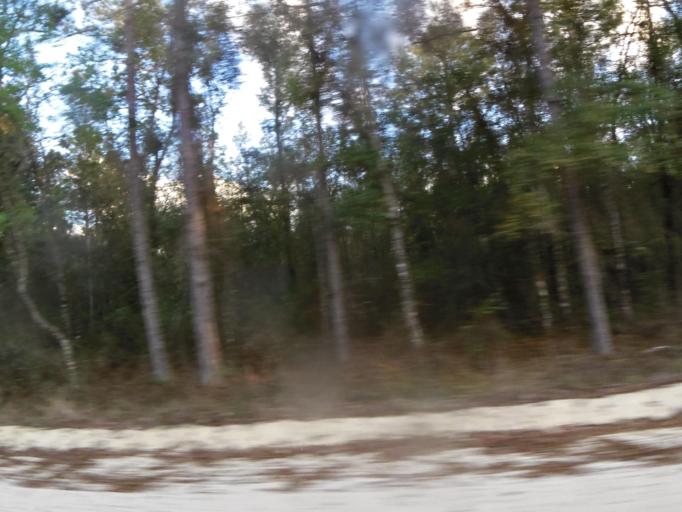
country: US
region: Florida
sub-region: Putnam County
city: Interlachen
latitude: 29.7796
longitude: -81.8462
